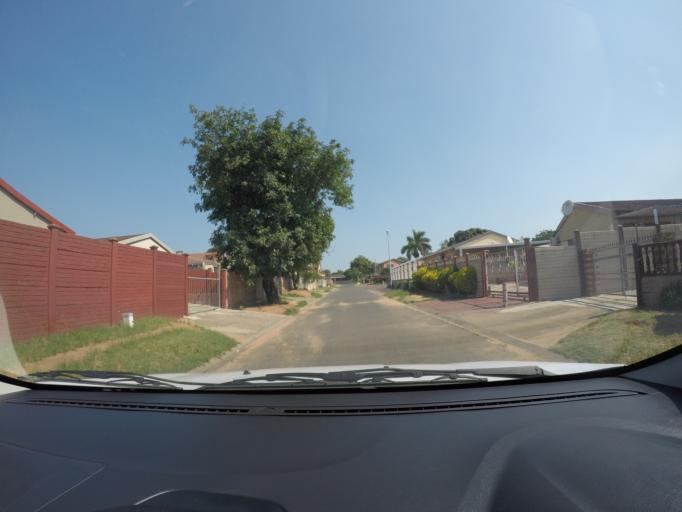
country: ZA
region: KwaZulu-Natal
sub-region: uThungulu District Municipality
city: Richards Bay
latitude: -28.7209
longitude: 32.0451
